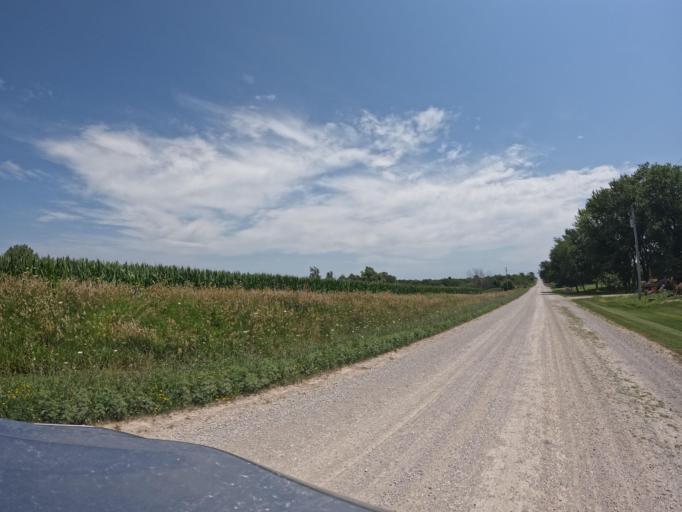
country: US
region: Iowa
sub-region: Appanoose County
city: Centerville
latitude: 40.7867
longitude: -92.9346
